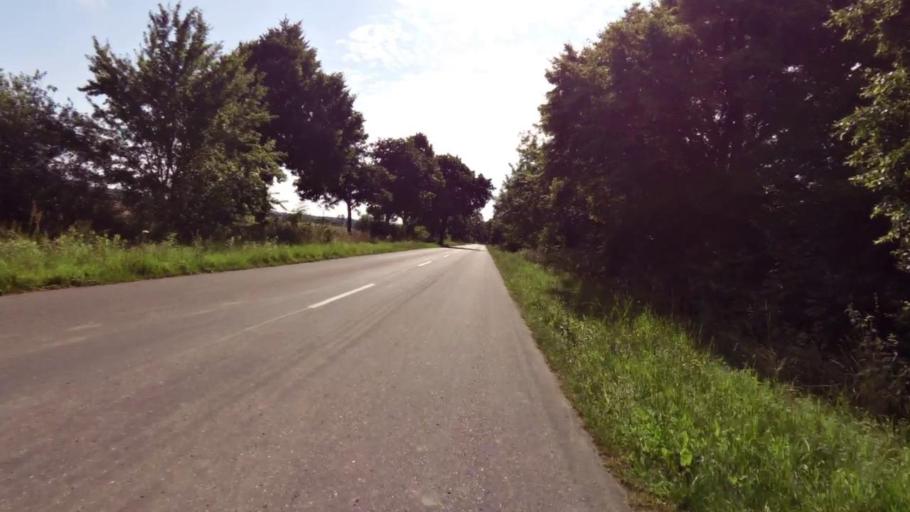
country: PL
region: West Pomeranian Voivodeship
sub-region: Powiat stargardzki
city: Dobrzany
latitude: 53.3644
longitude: 15.4113
